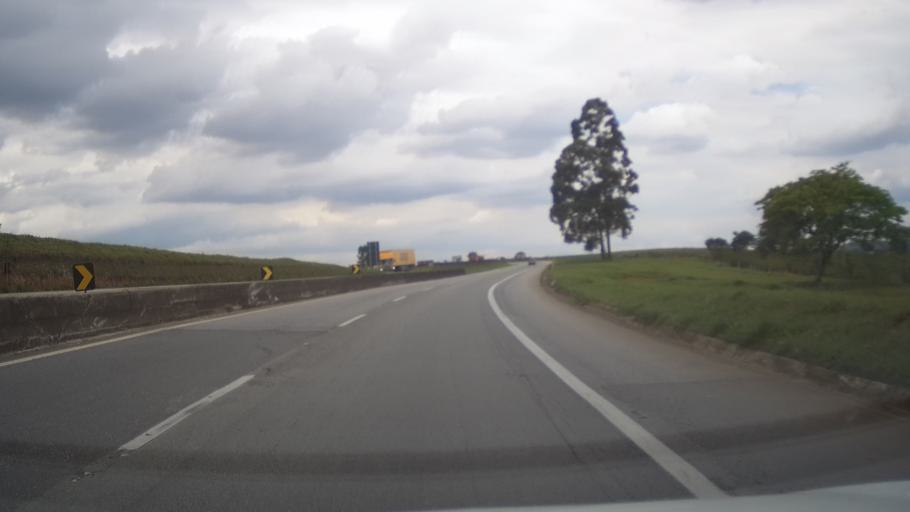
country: BR
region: Minas Gerais
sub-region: Tres Coracoes
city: Tres Coracoes
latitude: -21.4912
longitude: -45.2096
